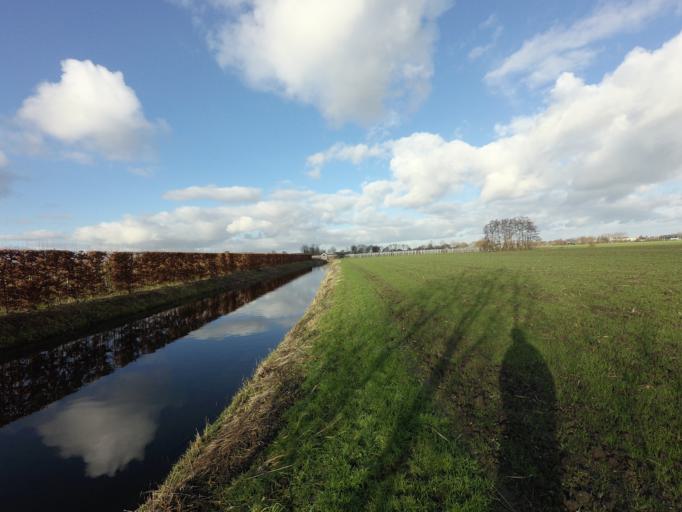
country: NL
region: Utrecht
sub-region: Gemeente Lopik
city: Lopik
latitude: 51.9999
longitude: 4.9594
